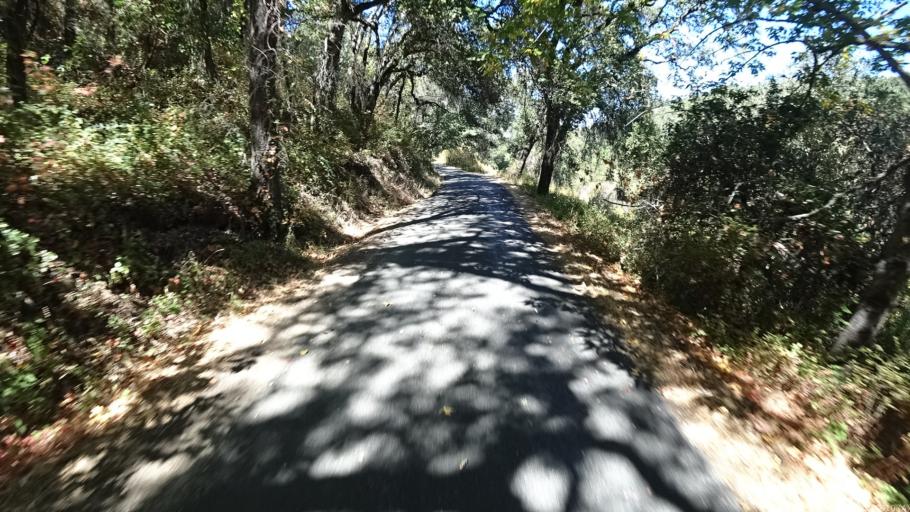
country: US
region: California
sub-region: Monterey County
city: Carmel Valley Village
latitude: 36.4320
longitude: -121.7906
